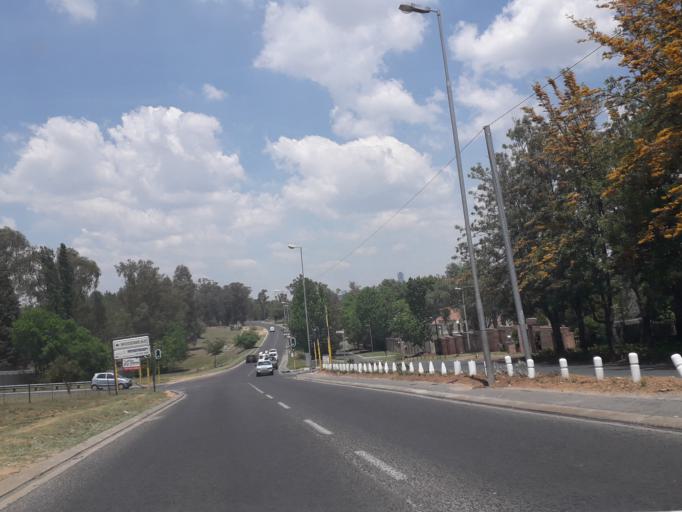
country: ZA
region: Gauteng
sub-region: City of Johannesburg Metropolitan Municipality
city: Midrand
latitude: -26.0417
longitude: 28.0697
